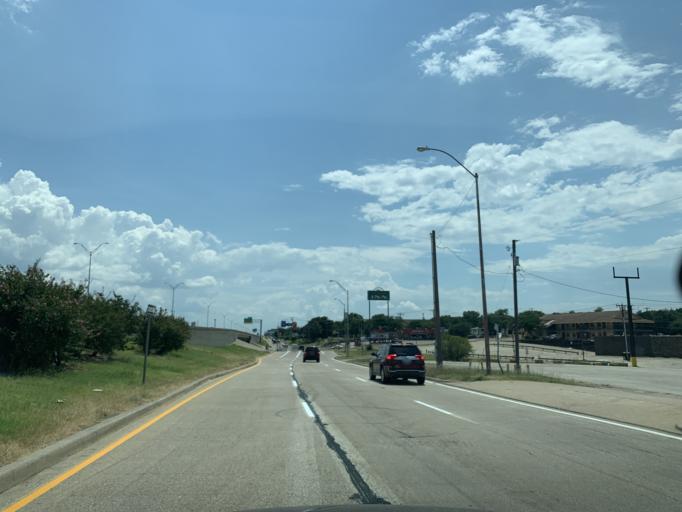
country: US
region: Texas
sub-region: Tarrant County
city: Edgecliff Village
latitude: 32.6553
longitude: -97.3217
